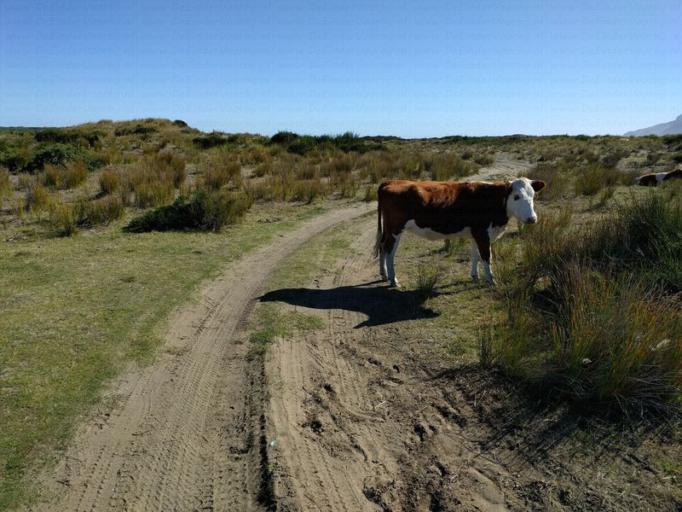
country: CL
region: Los Lagos
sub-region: Provincia de Chiloe
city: Ancud
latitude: -42.0478
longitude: -74.0228
